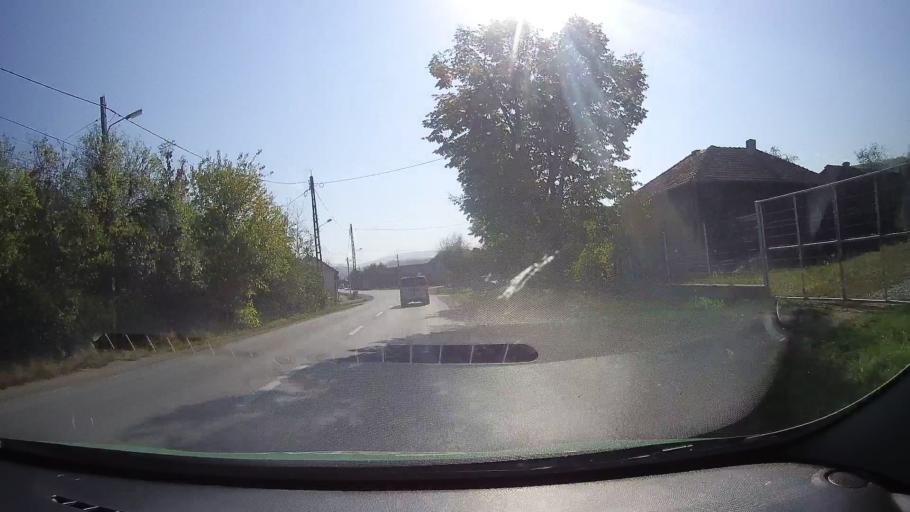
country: RO
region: Hunedoara
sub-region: Comuna Dobra
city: Dobra
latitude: 45.9171
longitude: 22.5608
